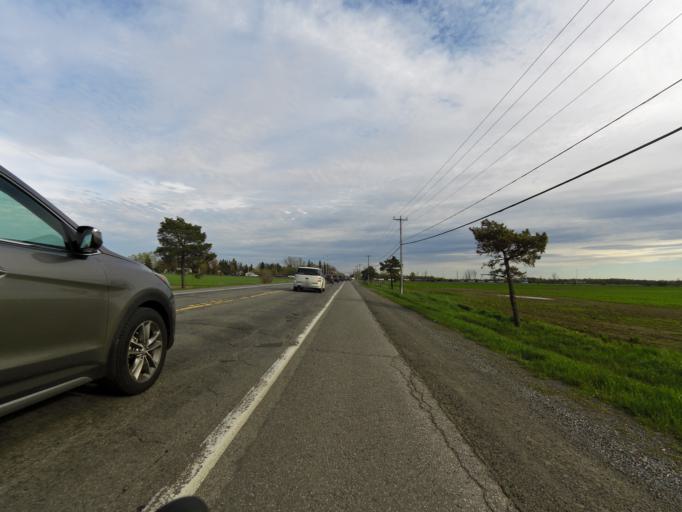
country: CA
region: Ontario
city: Ottawa
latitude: 45.3089
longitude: -75.7095
